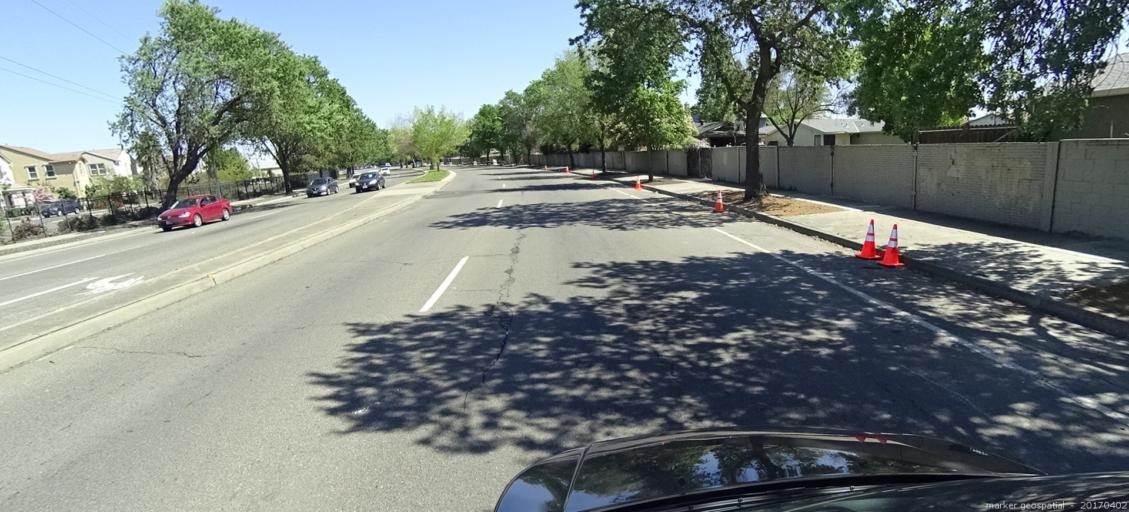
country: US
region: California
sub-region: Sacramento County
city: Parkway
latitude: 38.4745
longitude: -121.4579
